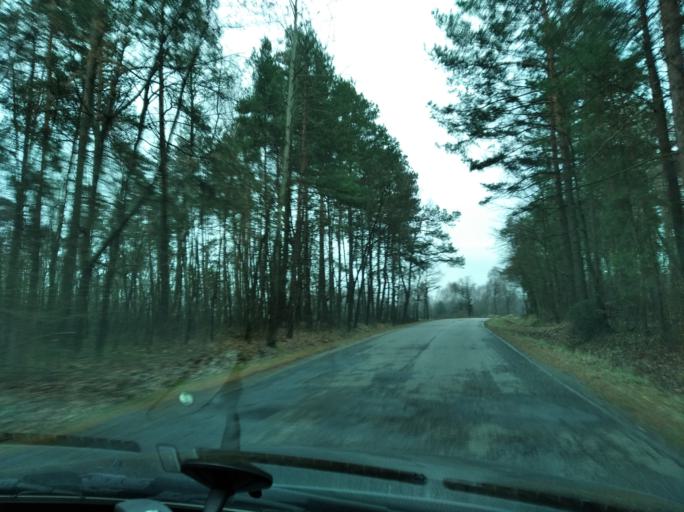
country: PL
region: Subcarpathian Voivodeship
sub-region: Powiat lancucki
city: Zolynia
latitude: 50.1873
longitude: 22.3087
